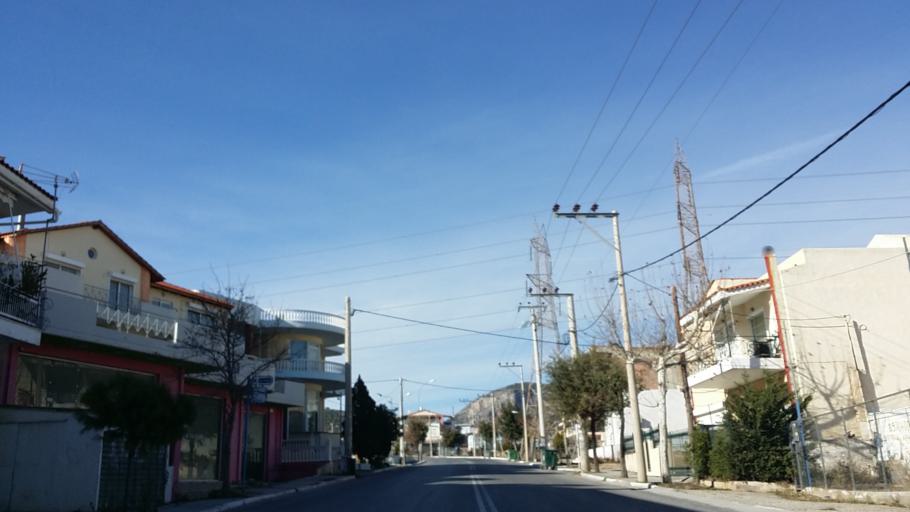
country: GR
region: Attica
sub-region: Nomarchia Dytikis Attikis
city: Ano Liosia
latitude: 38.0885
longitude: 23.6921
